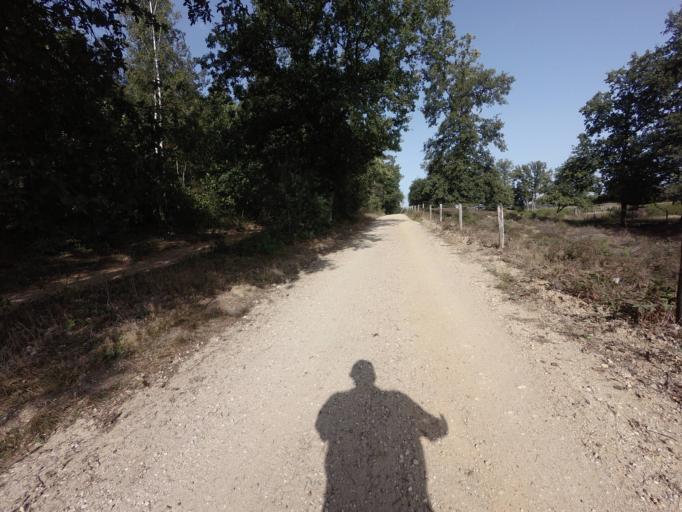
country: NL
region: Limburg
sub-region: Gemeente Roerdalen
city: Herkenbosch
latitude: 51.1800
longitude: 6.0759
